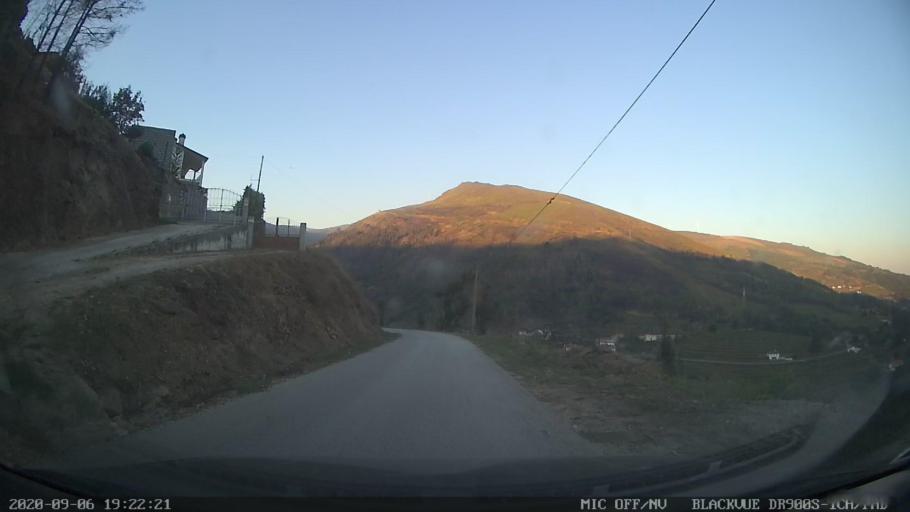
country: PT
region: Vila Real
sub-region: Mesao Frio
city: Mesao Frio
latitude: 41.1838
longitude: -7.9257
